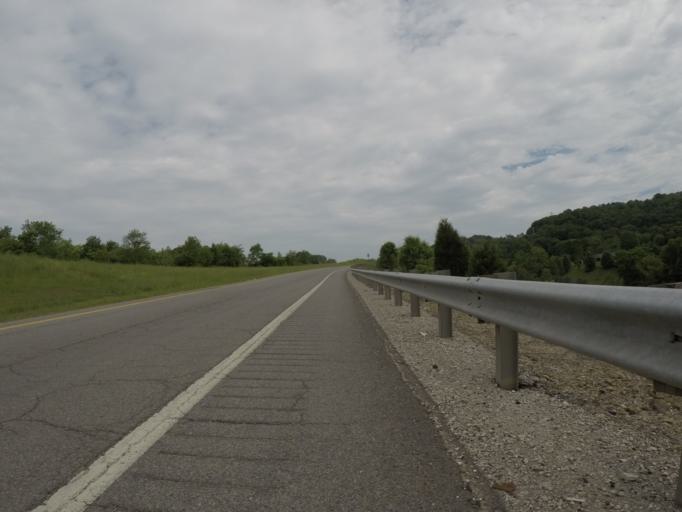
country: US
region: West Virginia
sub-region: Wayne County
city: Kenova
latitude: 38.3716
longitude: -82.5881
